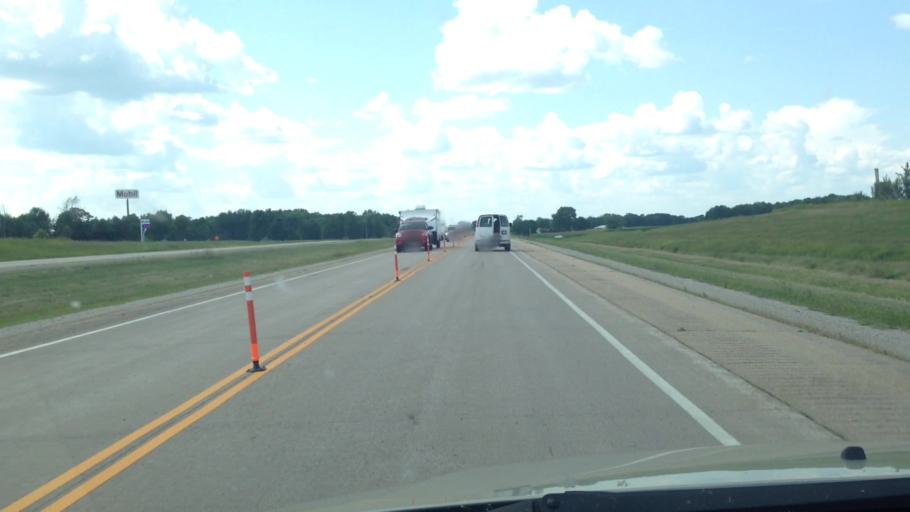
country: US
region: Wisconsin
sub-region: Brown County
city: Pulaski
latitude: 44.6920
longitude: -88.3336
